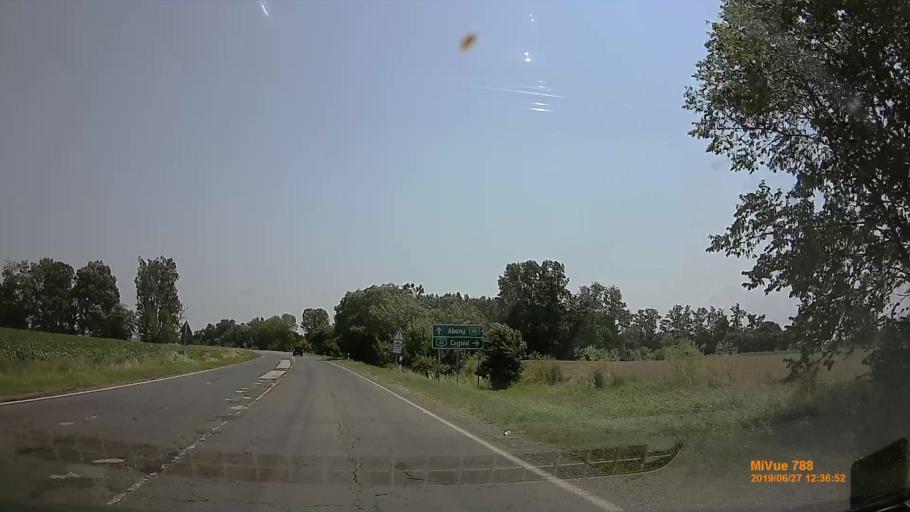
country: HU
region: Pest
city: Tortel
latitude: 47.1865
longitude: 19.9279
